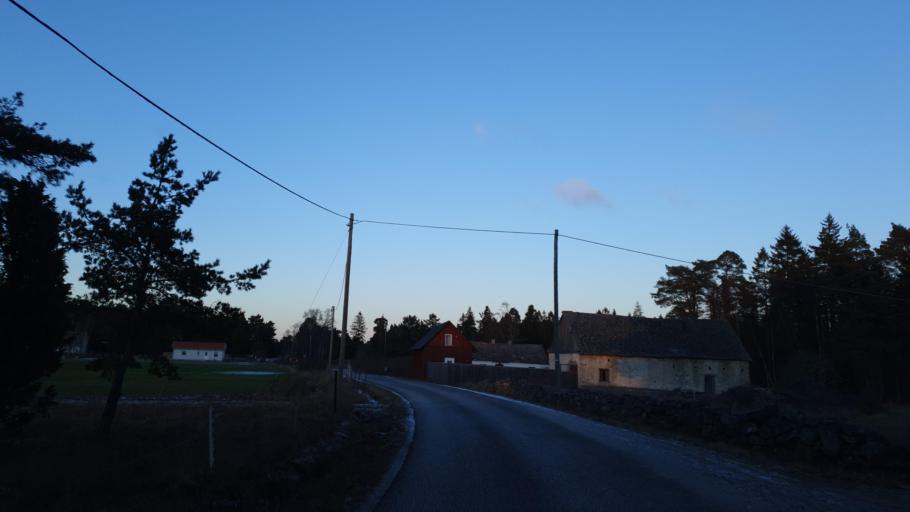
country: SE
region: Gotland
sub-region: Gotland
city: Slite
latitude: 57.3835
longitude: 18.8084
